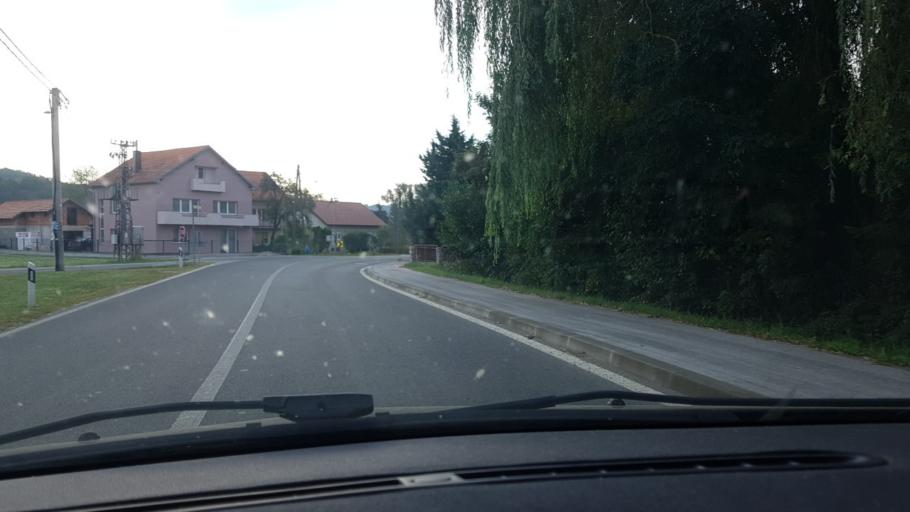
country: HR
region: Krapinsko-Zagorska
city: Zlatar
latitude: 46.1025
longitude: 16.0618
